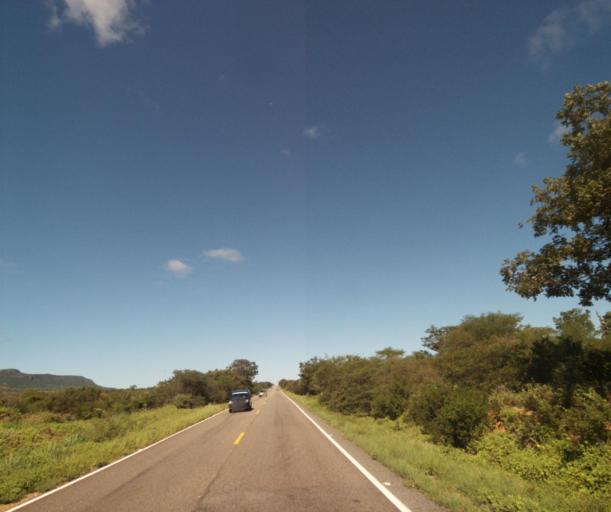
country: BR
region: Bahia
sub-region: Palmas De Monte Alto
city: Palmas de Monte Alto
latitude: -14.2448
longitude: -43.1037
